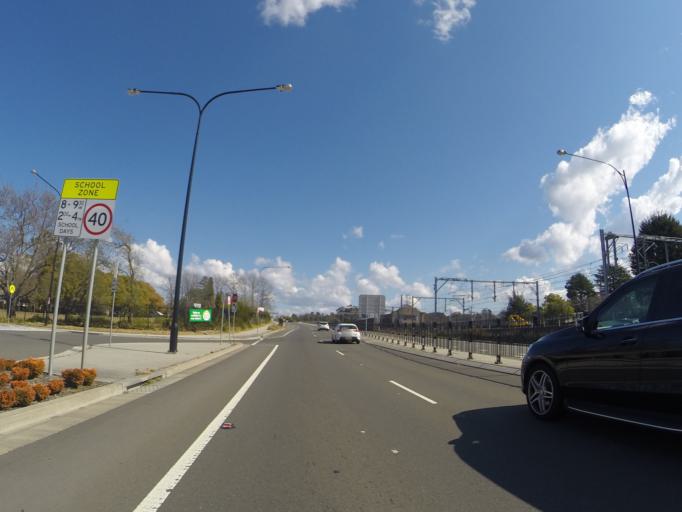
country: AU
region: New South Wales
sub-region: Blue Mountains Municipality
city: Lawson
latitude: -33.7201
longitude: 150.4286
